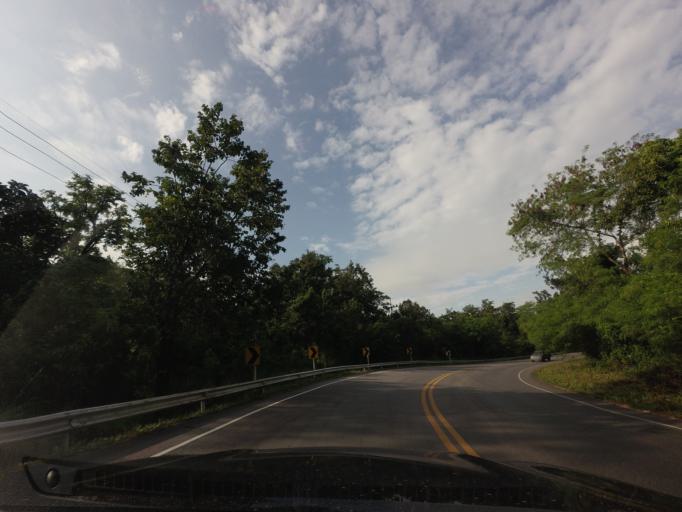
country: TH
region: Nong Khai
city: Pho Tak
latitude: 17.8046
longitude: 102.3246
